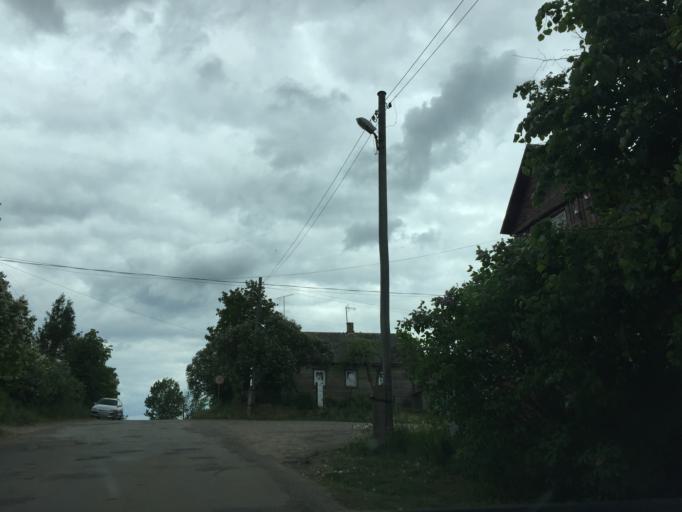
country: LV
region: Dagda
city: Dagda
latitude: 56.0894
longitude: 27.5361
